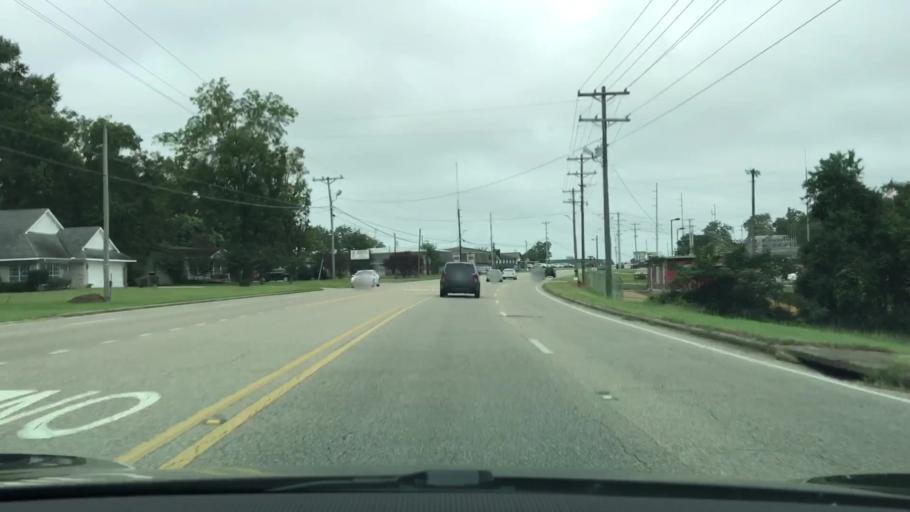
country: US
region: Alabama
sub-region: Pike County
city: Troy
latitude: 31.7800
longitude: -85.9638
